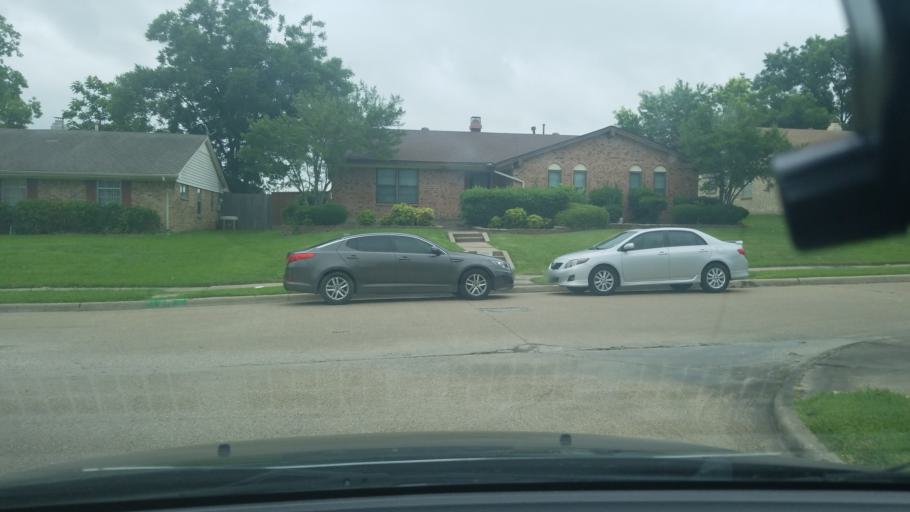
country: US
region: Texas
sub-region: Dallas County
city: Mesquite
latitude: 32.7810
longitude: -96.6313
